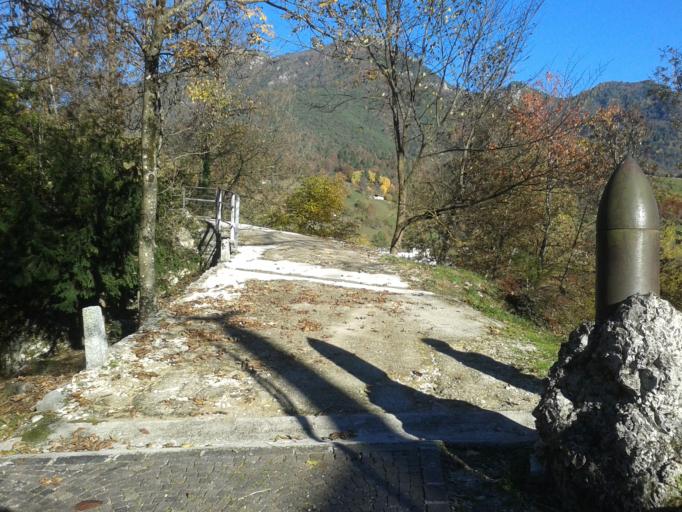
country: IT
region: Trentino-Alto Adige
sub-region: Provincia di Trento
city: Pieve di Ledro
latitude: 45.8971
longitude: 10.7208
